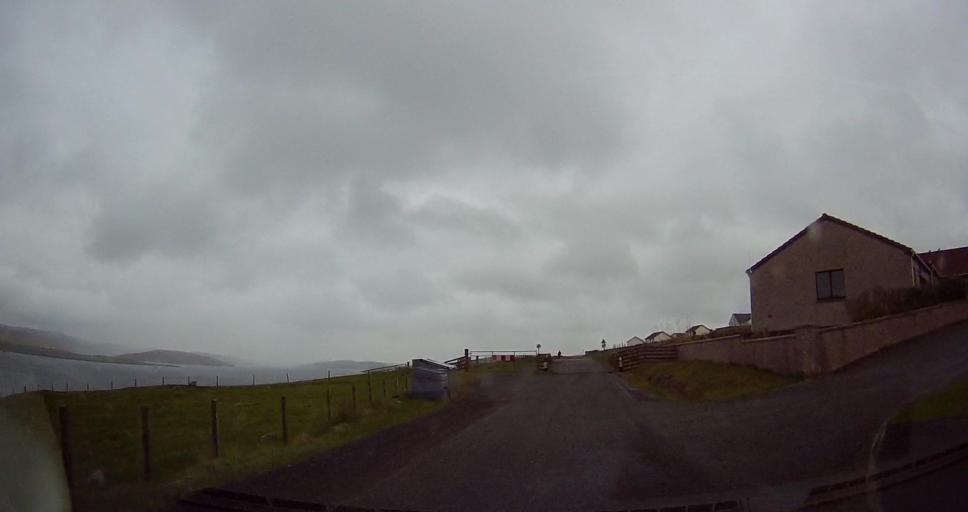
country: GB
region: Scotland
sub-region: Shetland Islands
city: Lerwick
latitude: 60.3894
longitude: -1.3701
